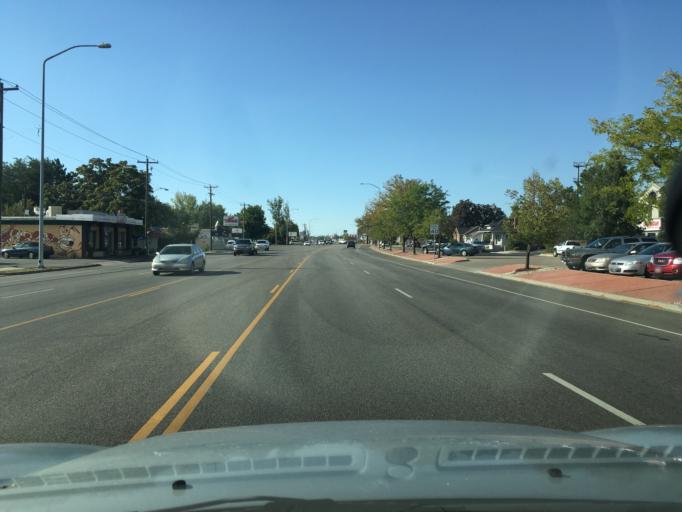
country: US
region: Utah
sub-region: Davis County
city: Layton
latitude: 41.0626
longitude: -111.9684
